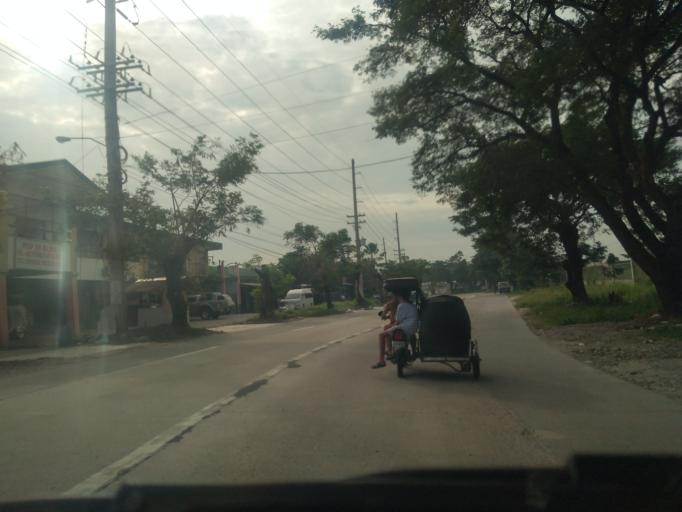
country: PH
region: Central Luzon
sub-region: Province of Pampanga
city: Calibutbut
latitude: 15.1234
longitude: 120.5868
